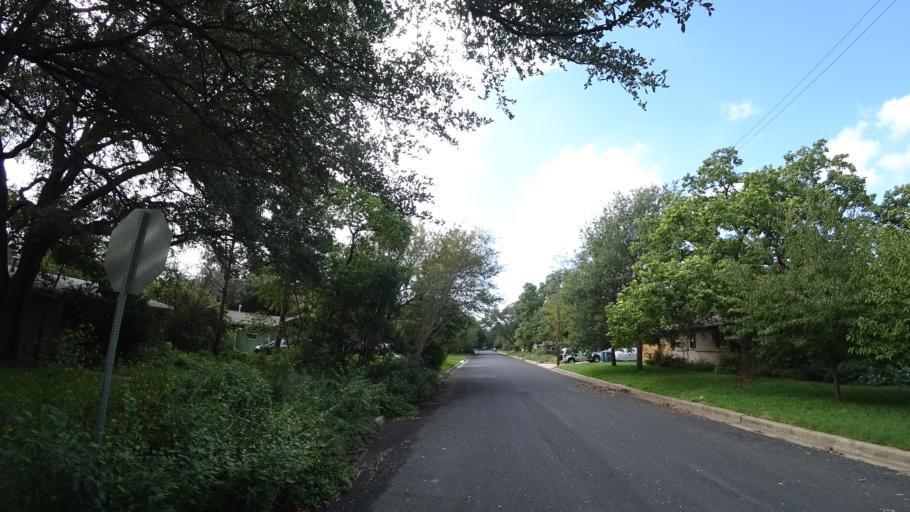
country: US
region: Texas
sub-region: Travis County
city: West Lake Hills
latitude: 30.3427
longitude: -97.7433
